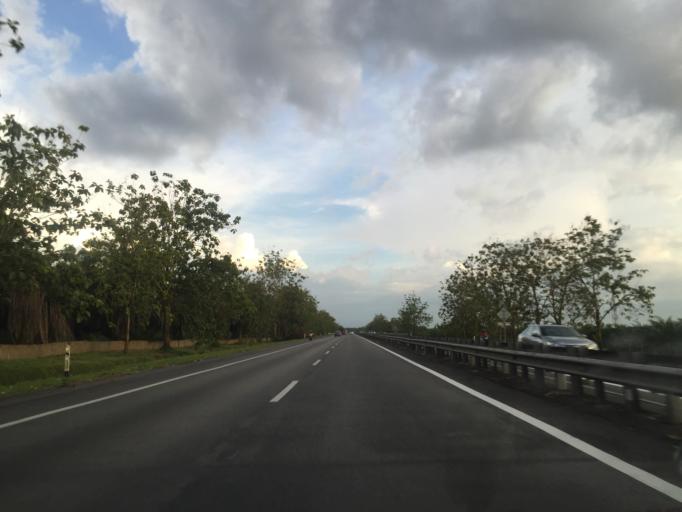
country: MY
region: Kedah
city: Bedong
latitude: 5.7493
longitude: 100.5118
